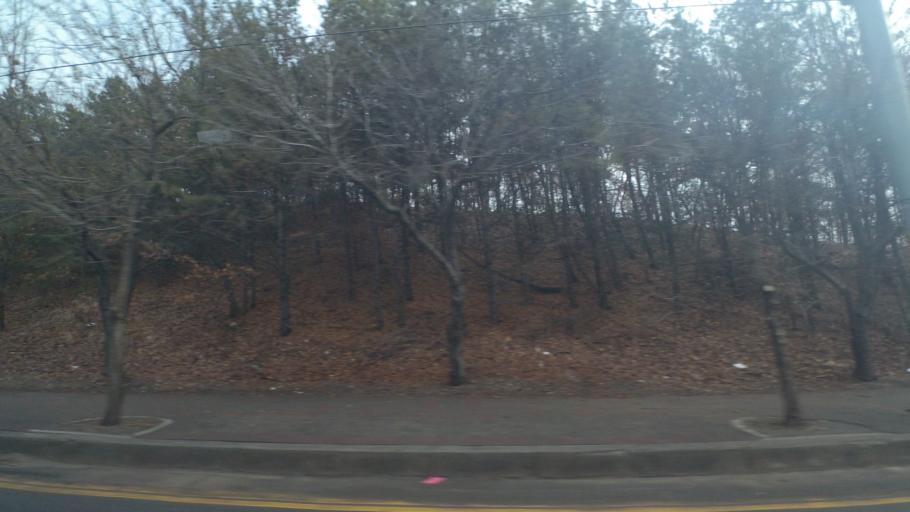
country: KR
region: Gyeonggi-do
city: Hwaseong-si
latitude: 36.9892
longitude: 126.8529
